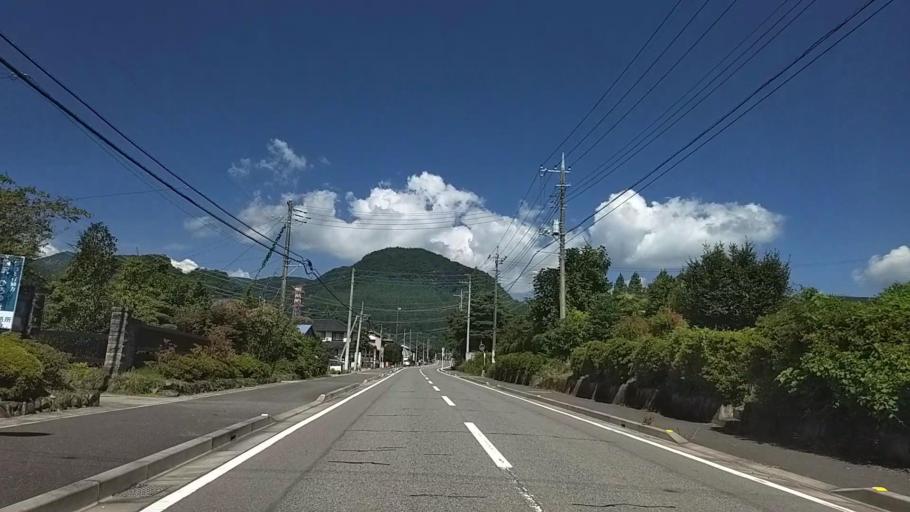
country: JP
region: Gunma
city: Annaka
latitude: 36.3459
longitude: 138.7216
